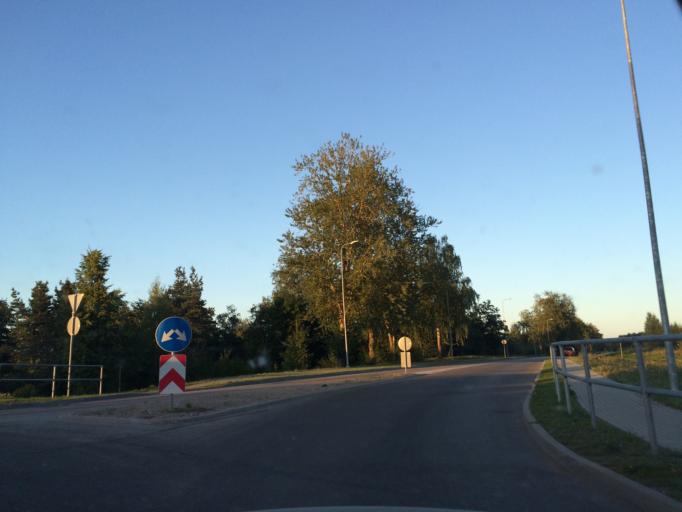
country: LV
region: Rezekne
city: Rezekne
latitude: 56.5125
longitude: 27.3583
